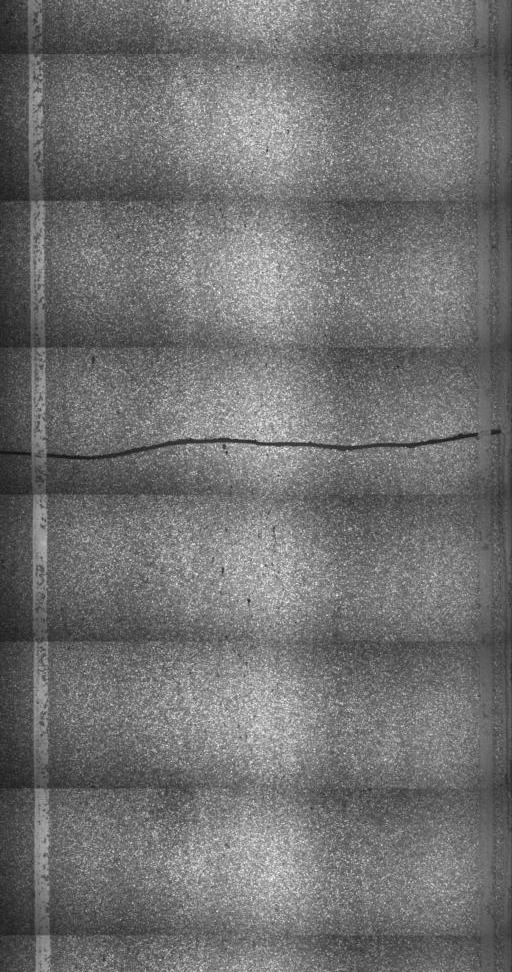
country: US
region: Vermont
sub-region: Franklin County
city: Richford
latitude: 44.9464
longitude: -72.7059
